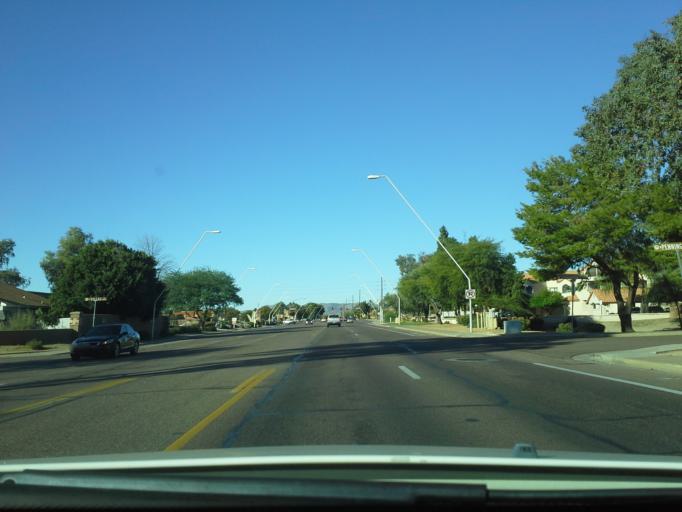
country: US
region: Arizona
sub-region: Maricopa County
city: San Carlos
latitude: 33.3496
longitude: -111.8728
